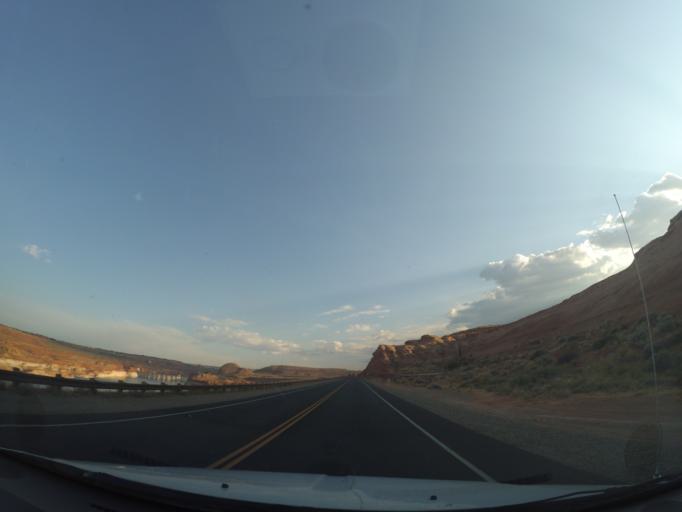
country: US
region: Arizona
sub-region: Coconino County
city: Page
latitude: 36.9531
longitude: -111.4929
